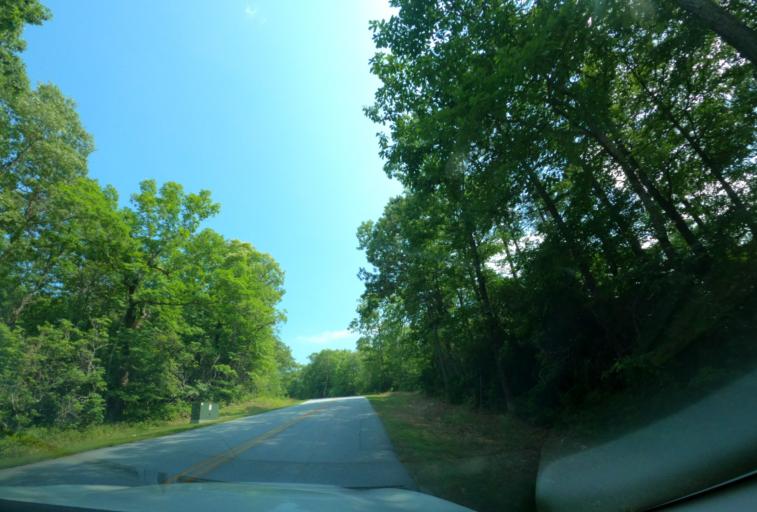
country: US
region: North Carolina
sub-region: Transylvania County
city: Brevard
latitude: 35.1001
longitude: -82.9555
